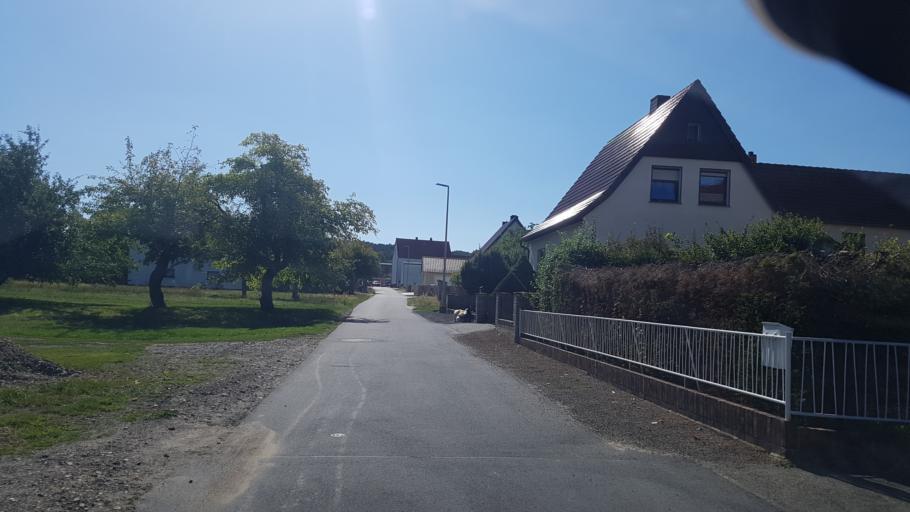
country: DE
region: Brandenburg
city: Hirschfeld
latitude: 51.3893
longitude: 13.6155
